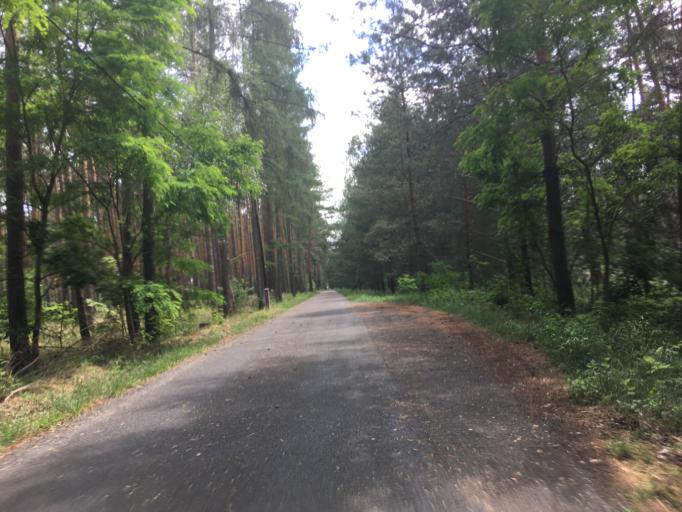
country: DE
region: Berlin
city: Muggelheim
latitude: 52.4019
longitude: 13.6487
